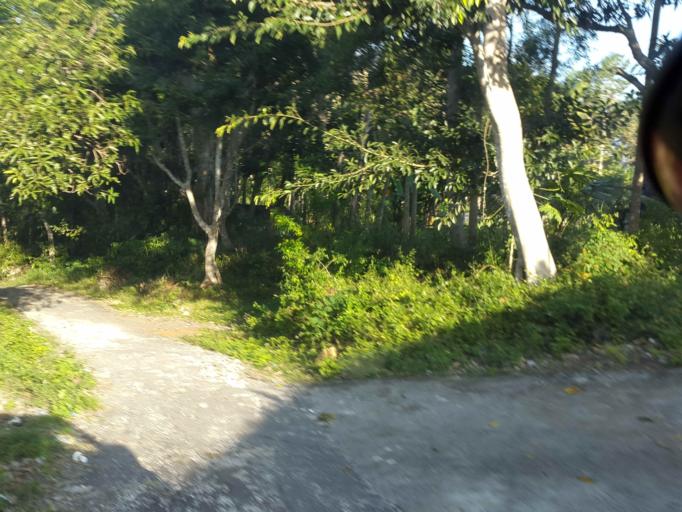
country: ID
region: Bali
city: Pejukutan
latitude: -8.7363
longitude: 115.5714
